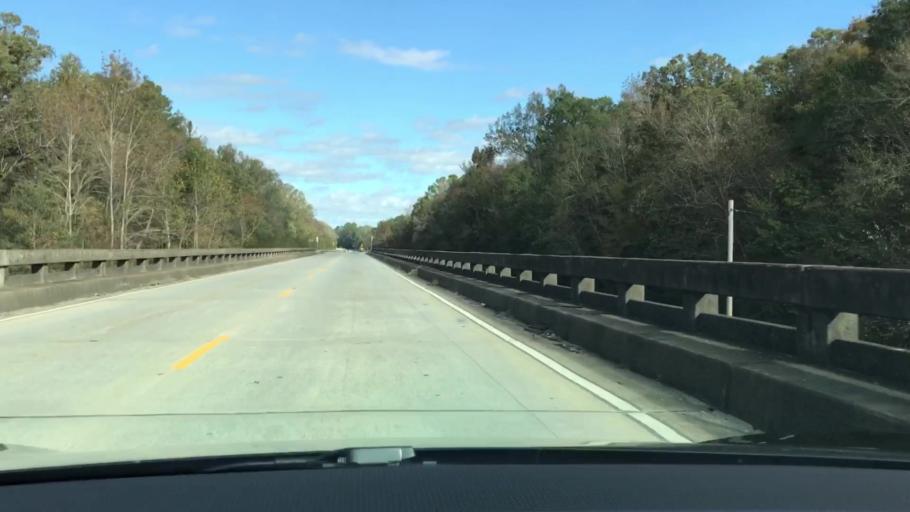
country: US
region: Georgia
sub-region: Jefferson County
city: Louisville
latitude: 32.9676
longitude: -82.3905
